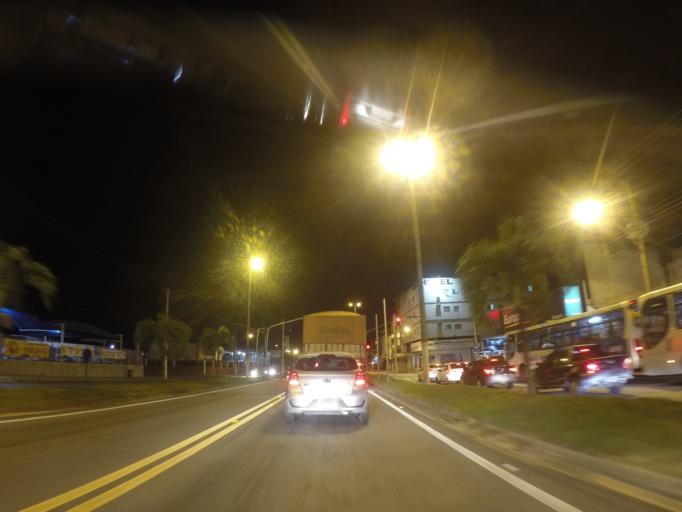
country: BR
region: Espirito Santo
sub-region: Linhares
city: Linhares
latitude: -19.3942
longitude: -40.0656
